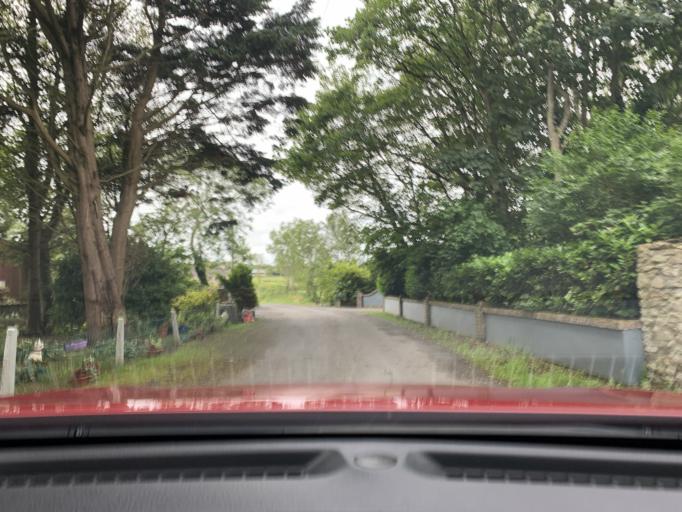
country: IE
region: Connaught
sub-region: Sligo
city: Sligo
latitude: 54.3761
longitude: -8.5215
